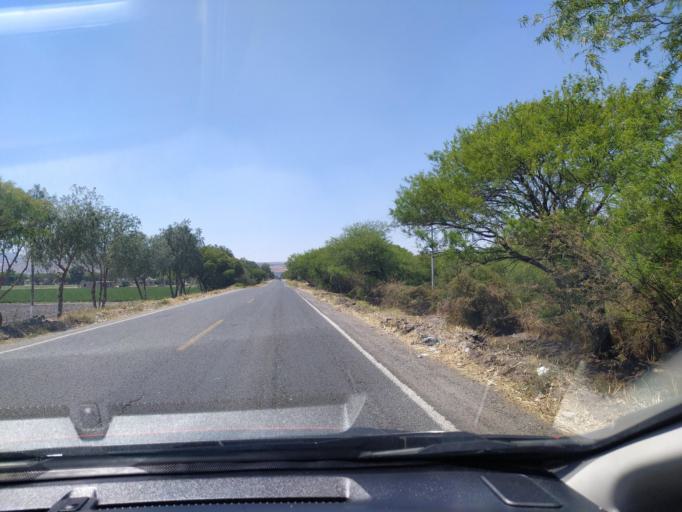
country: MX
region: Guanajuato
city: Ciudad Manuel Doblado
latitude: 20.7409
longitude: -101.9217
